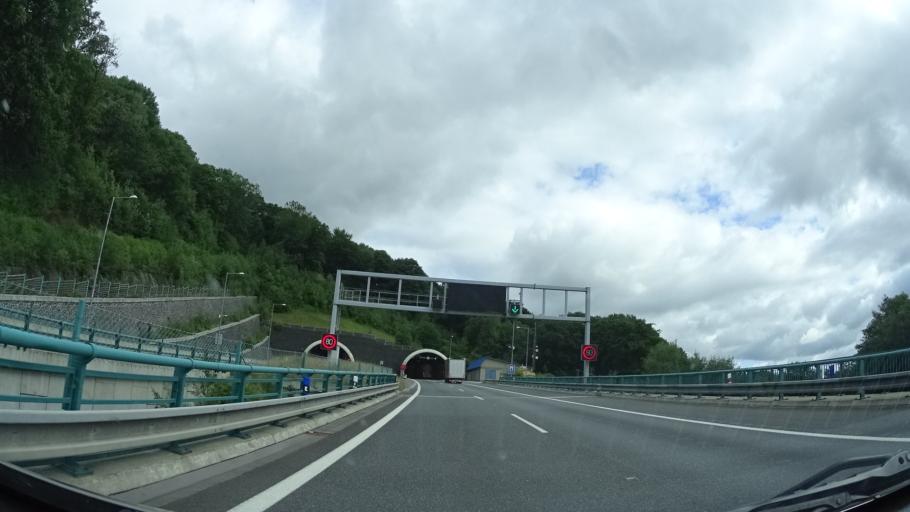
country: CZ
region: Ustecky
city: Libouchec
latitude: 50.7430
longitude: 14.0087
